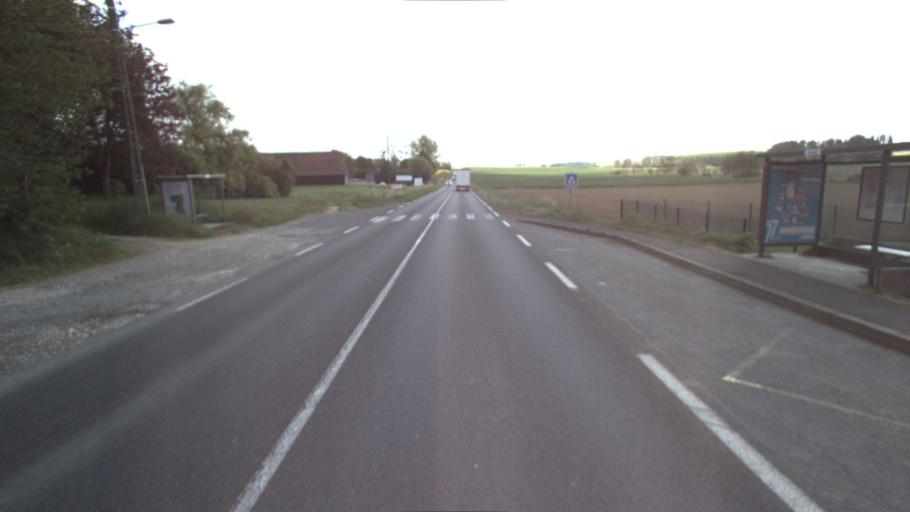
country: FR
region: Ile-de-France
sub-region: Departement de Seine-et-Marne
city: Choisy-en-Brie
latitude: 48.6991
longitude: 3.2683
